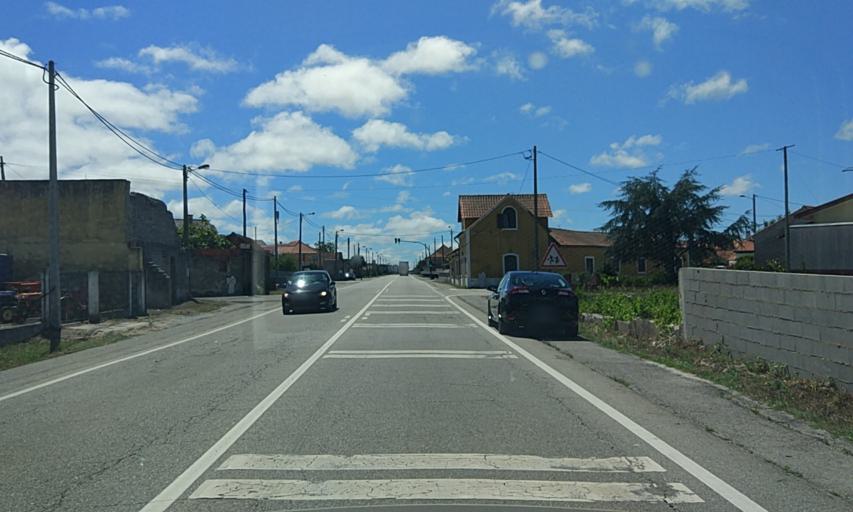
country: PT
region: Aveiro
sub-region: Vagos
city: Vagos
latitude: 40.4898
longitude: -8.6866
